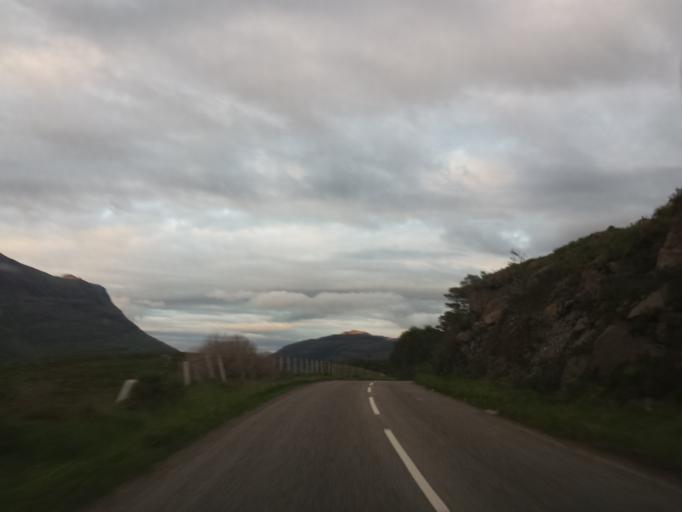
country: GB
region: Scotland
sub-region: Highland
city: Ullapool
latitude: 57.5278
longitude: -5.5573
